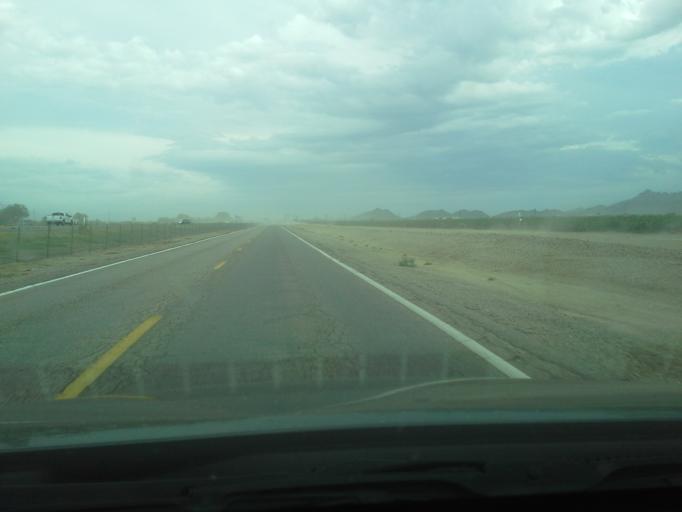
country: US
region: Arizona
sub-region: Pima County
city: Marana
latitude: 32.4440
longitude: -111.1916
